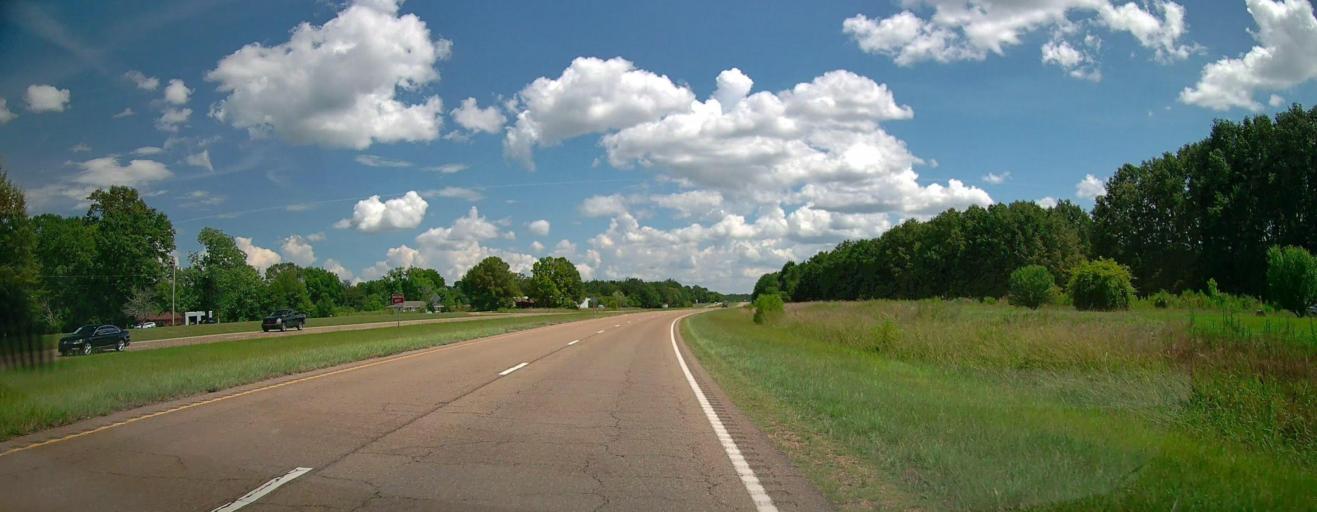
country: US
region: Mississippi
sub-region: Monroe County
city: Aberdeen
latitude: 33.8028
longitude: -88.4659
